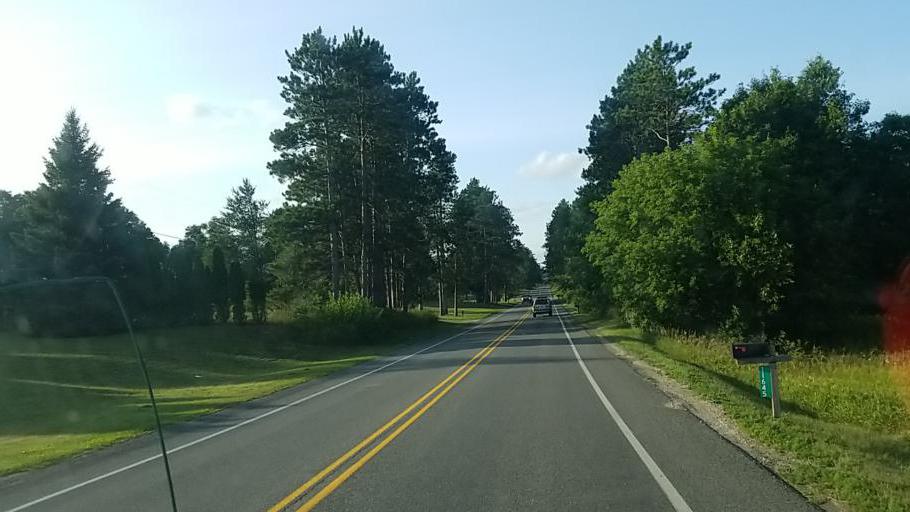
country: US
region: Michigan
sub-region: Montcalm County
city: Greenville
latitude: 43.1771
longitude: -85.3527
